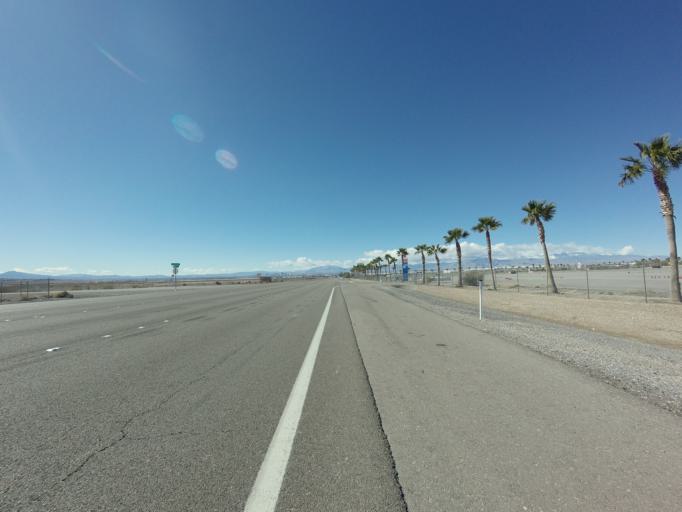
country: US
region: Nevada
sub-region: Clark County
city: Nellis Air Force Base
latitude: 36.2669
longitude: -115.0093
